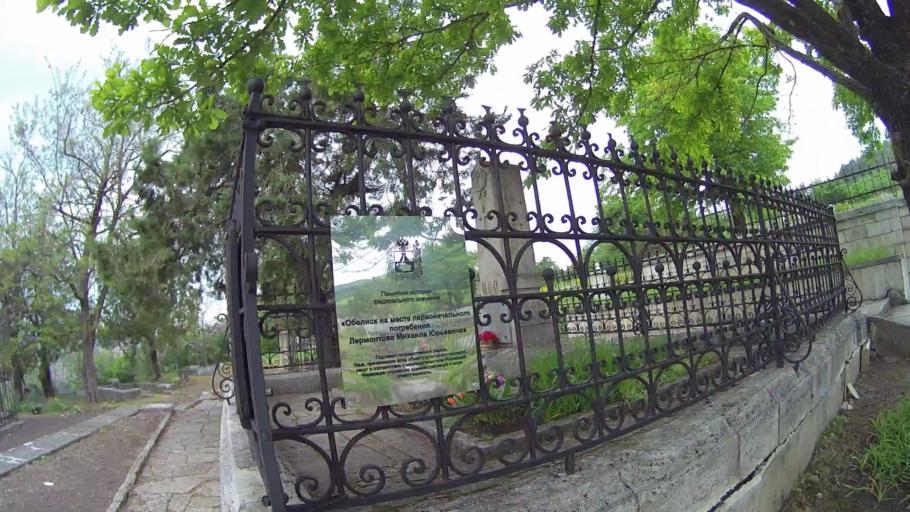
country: RU
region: Stavropol'skiy
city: Pyatigorsk
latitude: 44.0465
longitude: 43.0732
